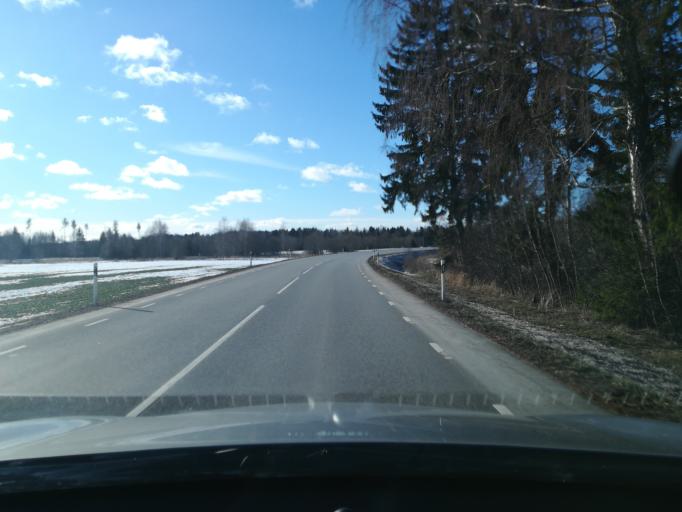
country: EE
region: Harju
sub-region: Saku vald
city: Saku
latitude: 59.2740
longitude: 24.6926
